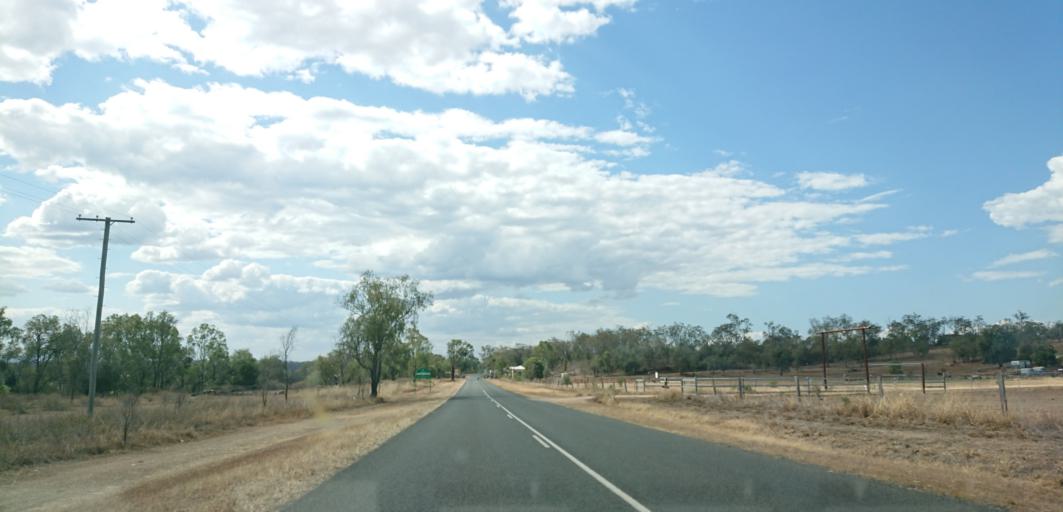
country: AU
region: Queensland
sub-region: Lockyer Valley
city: Gatton
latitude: -27.6348
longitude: 152.1862
